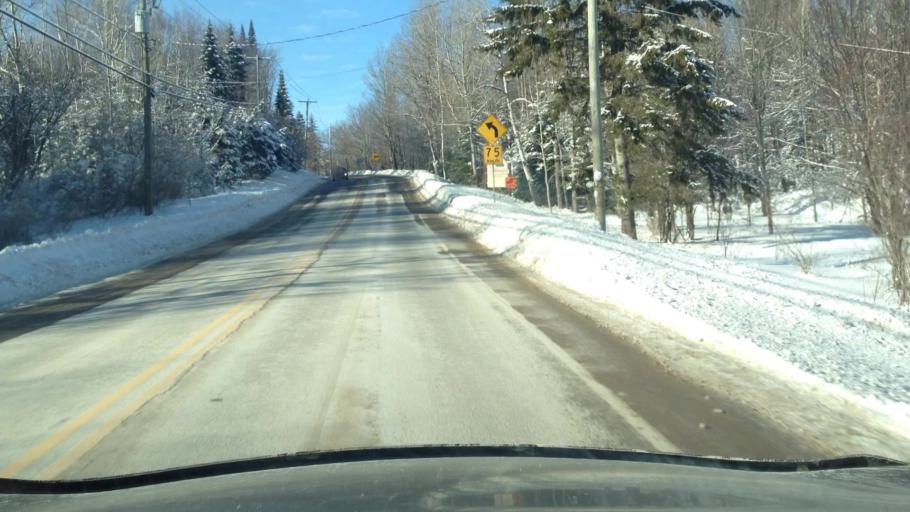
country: CA
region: Quebec
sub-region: Laurentides
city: Sainte-Agathe-des-Monts
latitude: 45.9336
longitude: -74.4346
